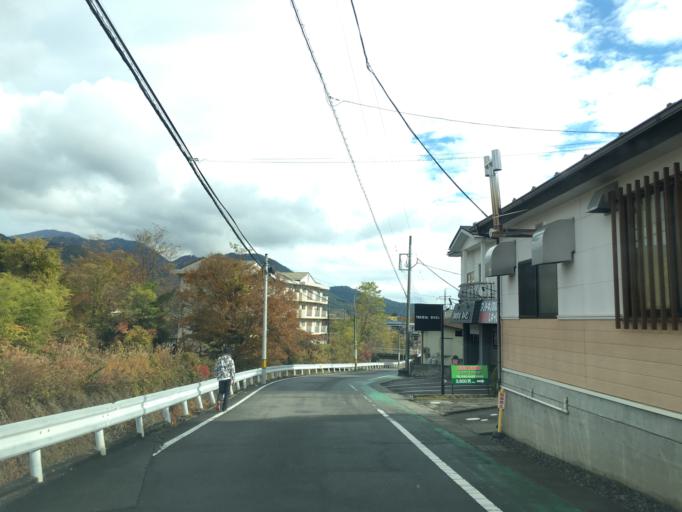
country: JP
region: Yamanashi
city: Fujikawaguchiko
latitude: 35.4852
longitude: 138.7831
